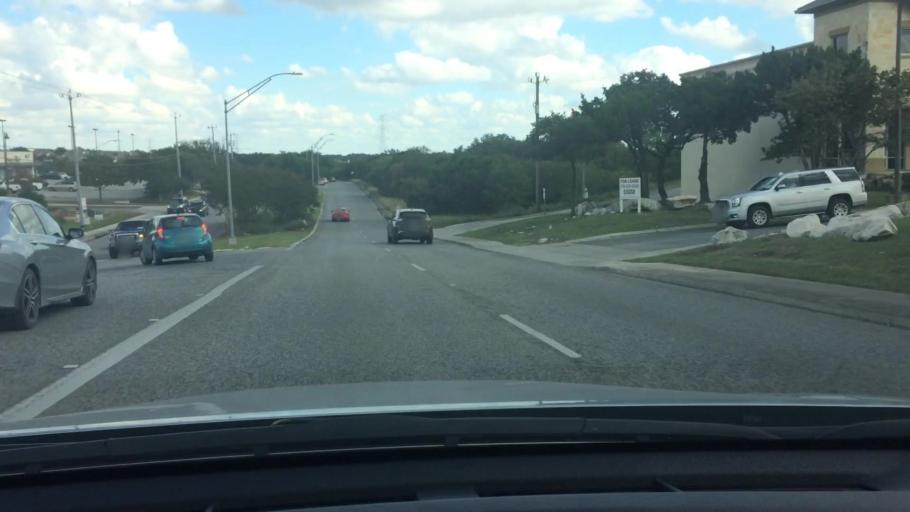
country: US
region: Texas
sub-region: Bexar County
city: Hollywood Park
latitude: 29.6361
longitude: -98.4545
